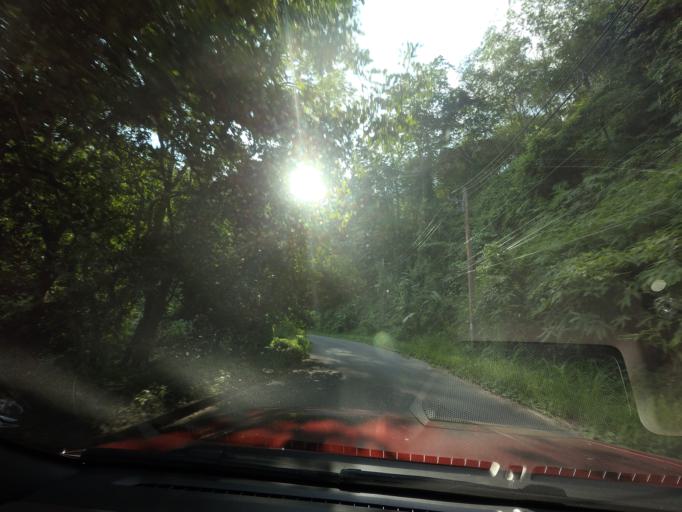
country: TH
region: Yala
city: Than To
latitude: 6.1430
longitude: 101.2908
